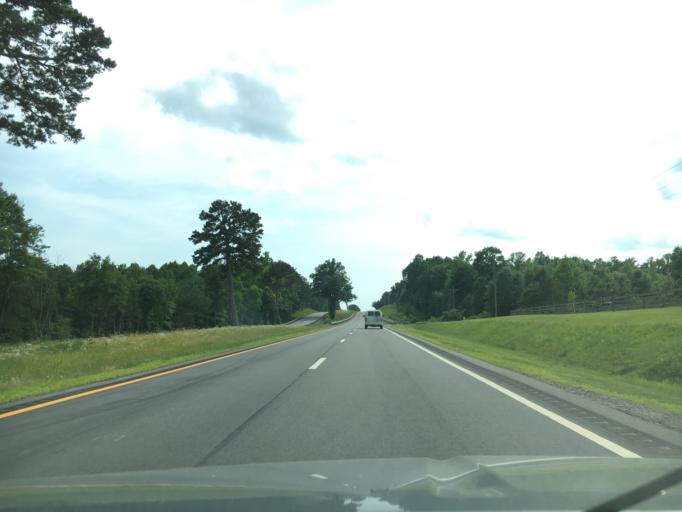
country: US
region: Virginia
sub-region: Mecklenburg County
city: Chase City
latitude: 36.9149
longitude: -78.5235
